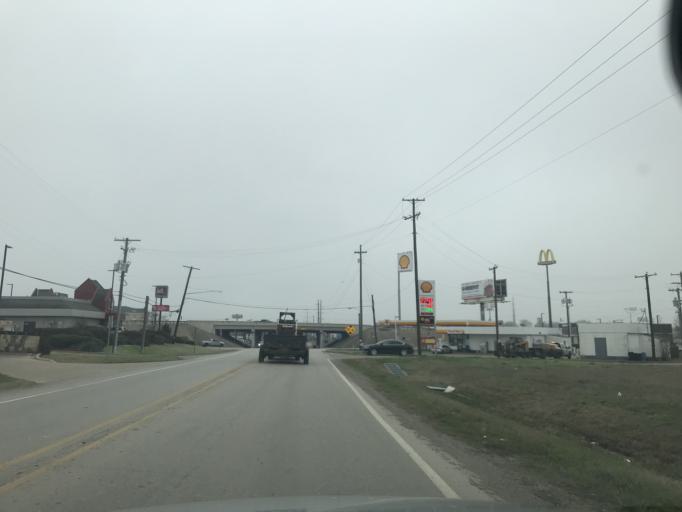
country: US
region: Texas
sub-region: Rockwall County
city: Royse City
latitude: 32.9709
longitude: -96.3320
